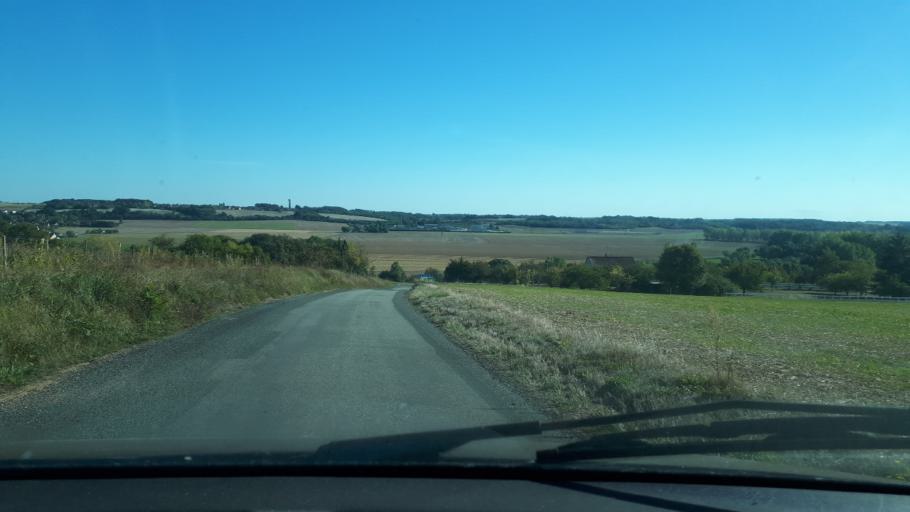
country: FR
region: Centre
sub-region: Departement du Loir-et-Cher
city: Naveil
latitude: 47.7982
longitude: 1.0198
